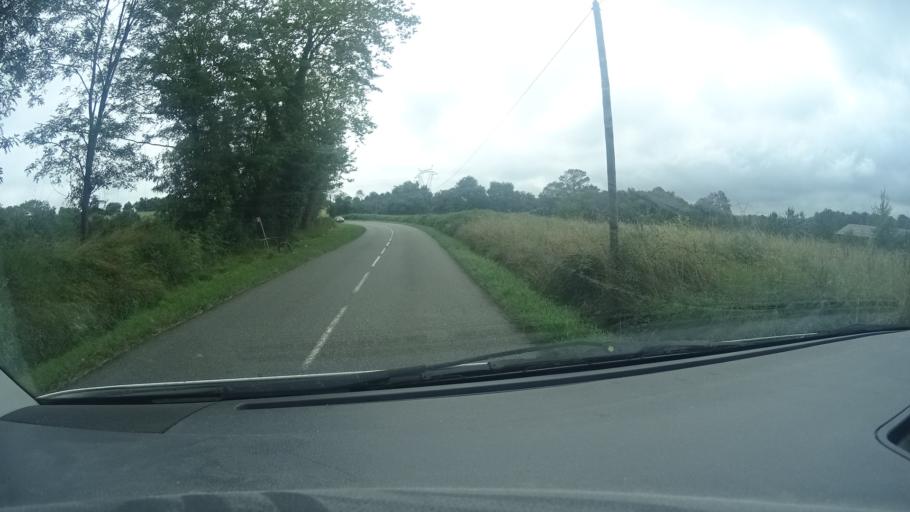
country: FR
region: Aquitaine
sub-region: Departement des Pyrenees-Atlantiques
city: Mont
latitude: 43.4894
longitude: -0.6752
